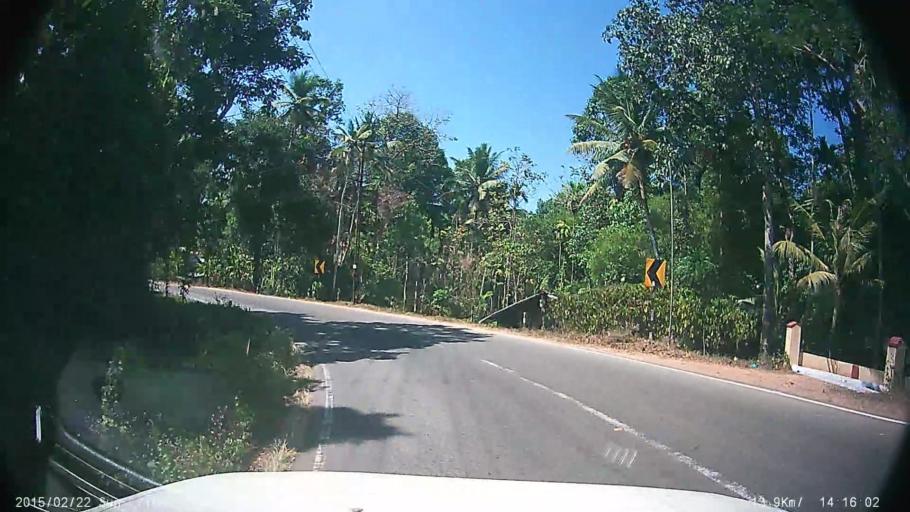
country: IN
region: Kerala
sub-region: Kottayam
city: Lalam
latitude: 9.5549
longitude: 76.6814
